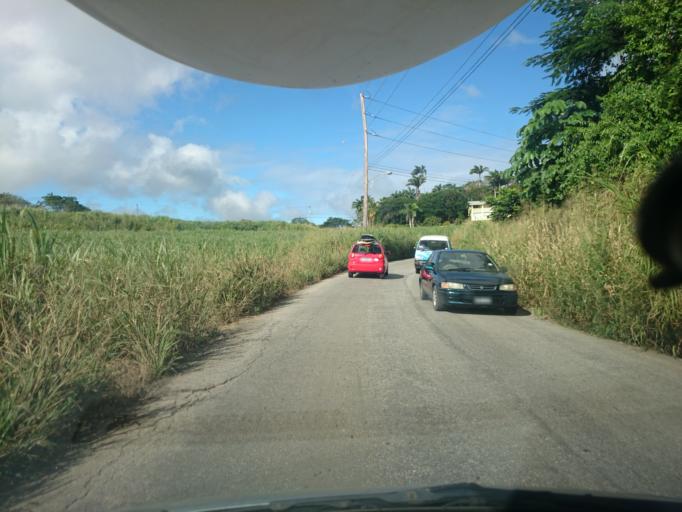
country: BB
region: Saint Thomas
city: Welchman Hall
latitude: 13.1673
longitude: -59.5527
